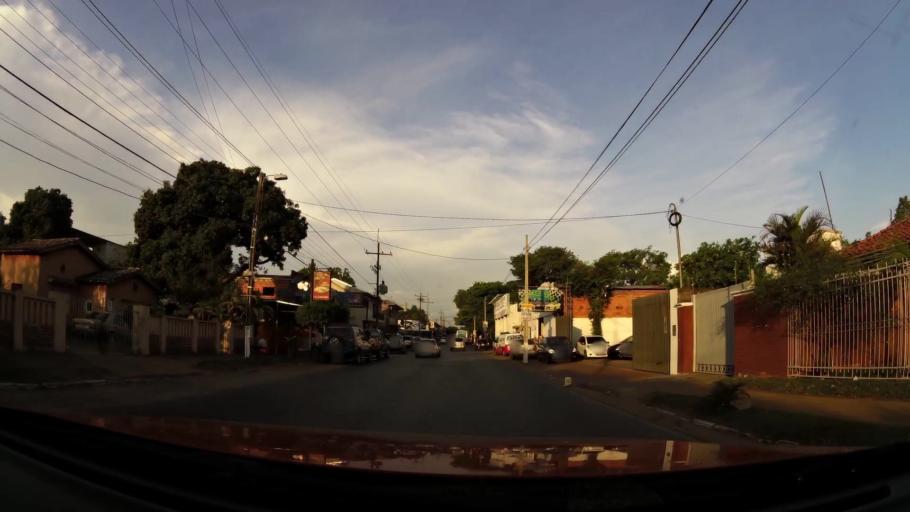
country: PY
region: Central
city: San Lorenzo
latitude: -25.3495
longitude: -57.5074
